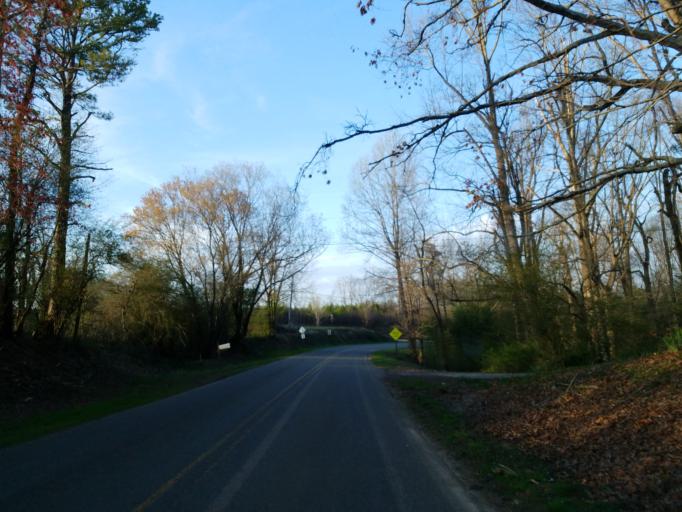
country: US
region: Georgia
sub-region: Pickens County
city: Jasper
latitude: 34.5045
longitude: -84.5223
